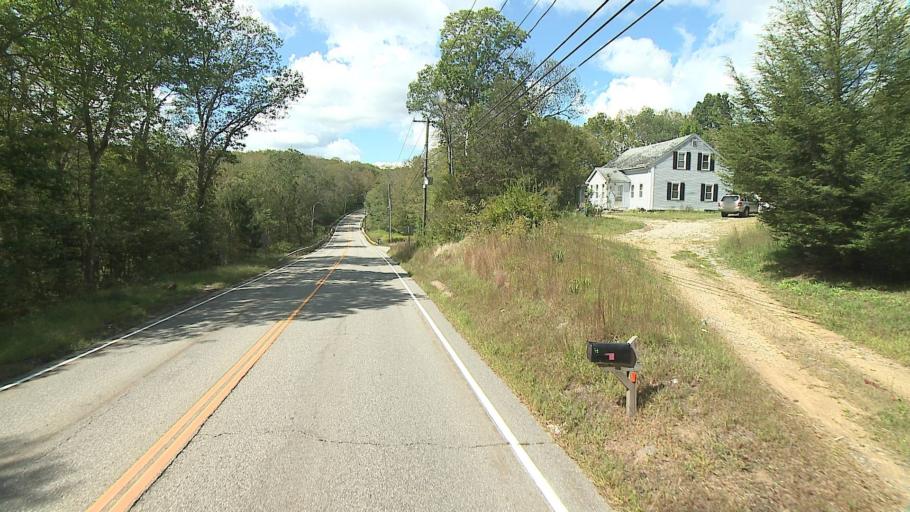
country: US
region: Connecticut
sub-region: Windham County
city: South Woodstock
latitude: 41.8793
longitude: -72.0982
